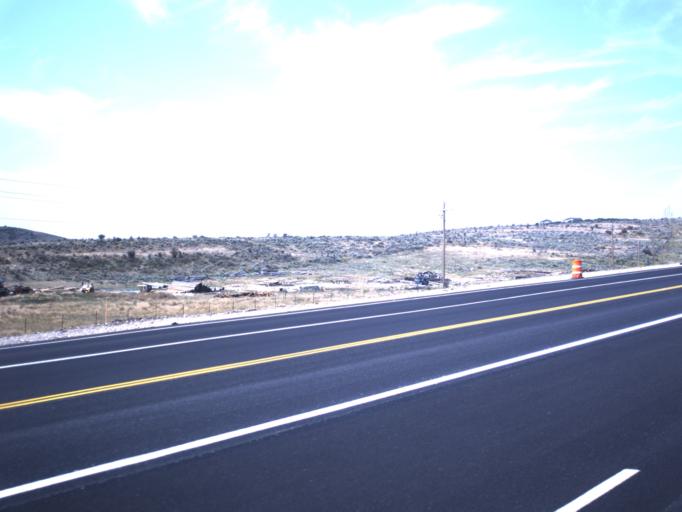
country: US
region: Utah
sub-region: Summit County
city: Kamas
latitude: 40.6401
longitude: -111.3203
